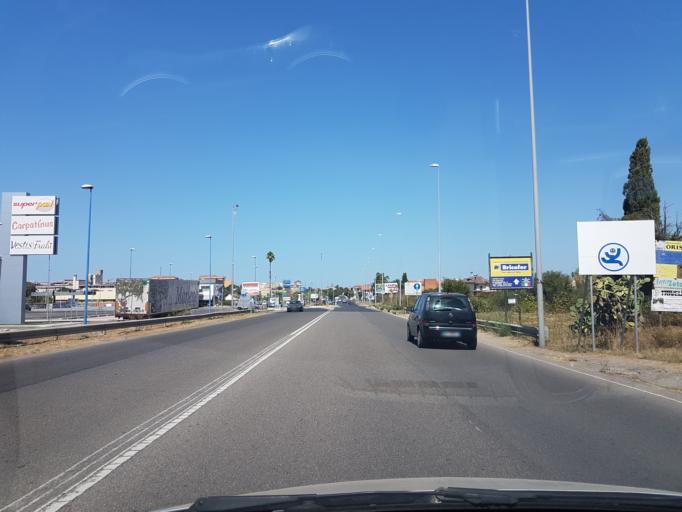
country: IT
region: Sardinia
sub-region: Provincia di Oristano
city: Santa Giusta
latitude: 39.8896
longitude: 8.6006
